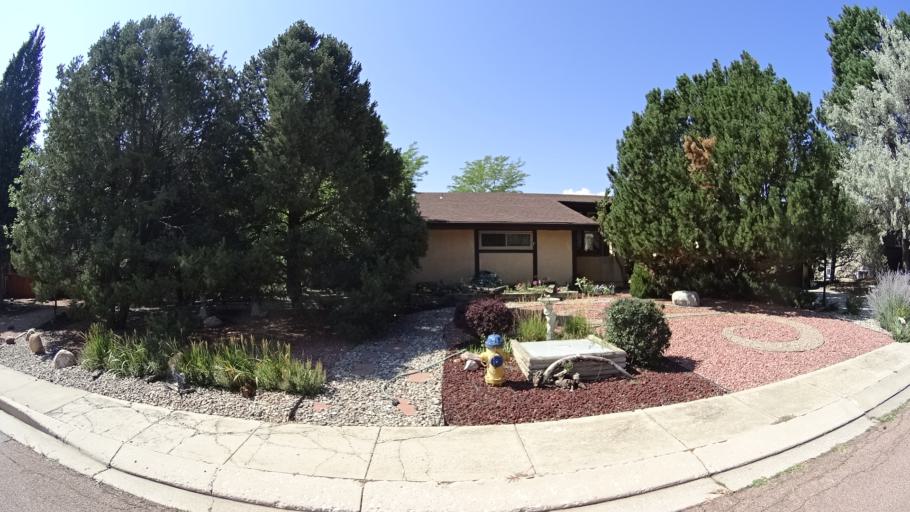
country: US
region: Colorado
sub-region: El Paso County
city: Air Force Academy
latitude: 38.9244
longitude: -104.8291
